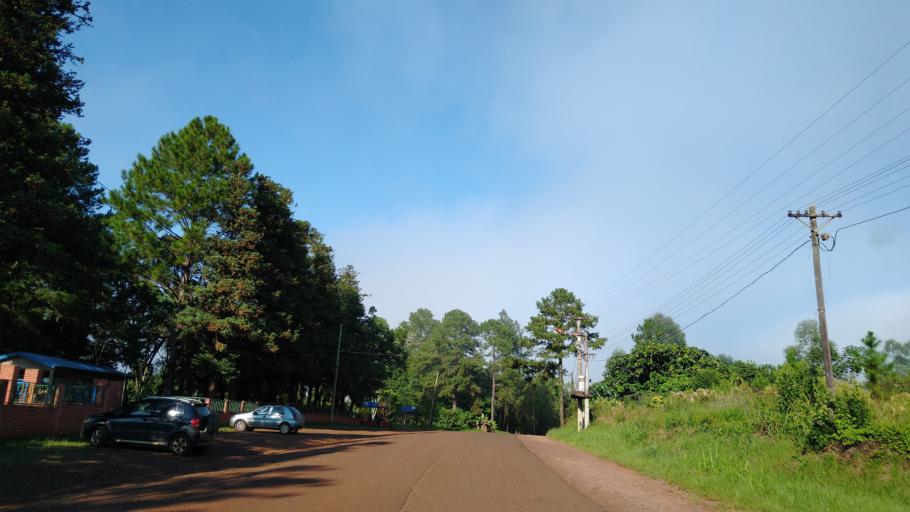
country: AR
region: Misiones
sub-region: Departamento de Montecarlo
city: Montecarlo
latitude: -26.5641
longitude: -54.7852
